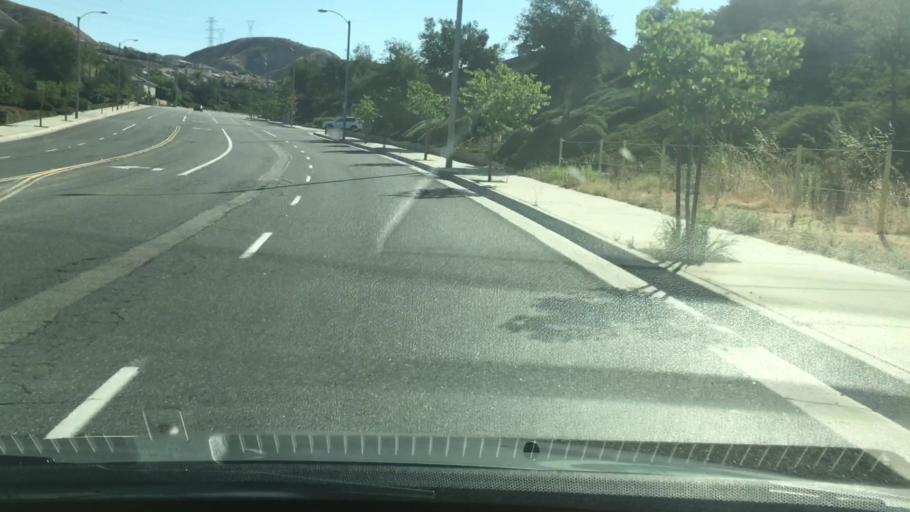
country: US
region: California
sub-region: Los Angeles County
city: Santa Clarita
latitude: 34.4600
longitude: -118.5088
